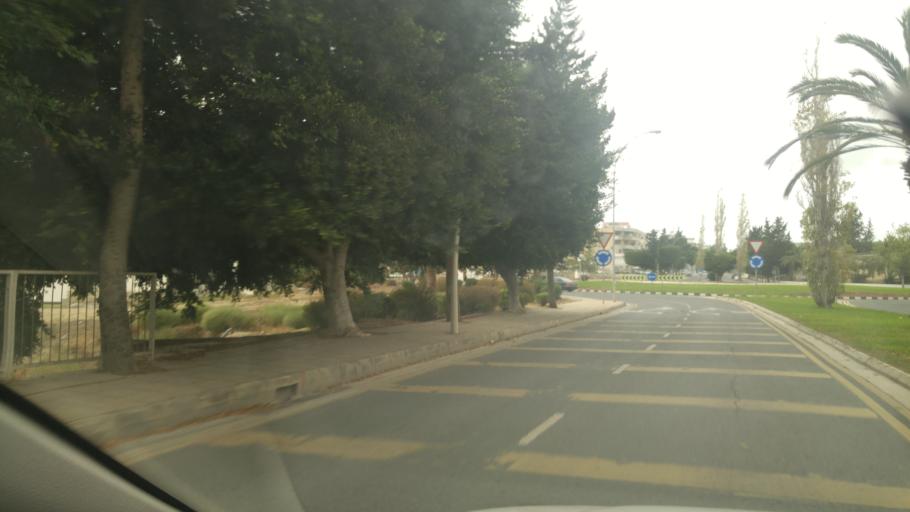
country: CY
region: Pafos
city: Paphos
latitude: 34.7677
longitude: 32.4416
